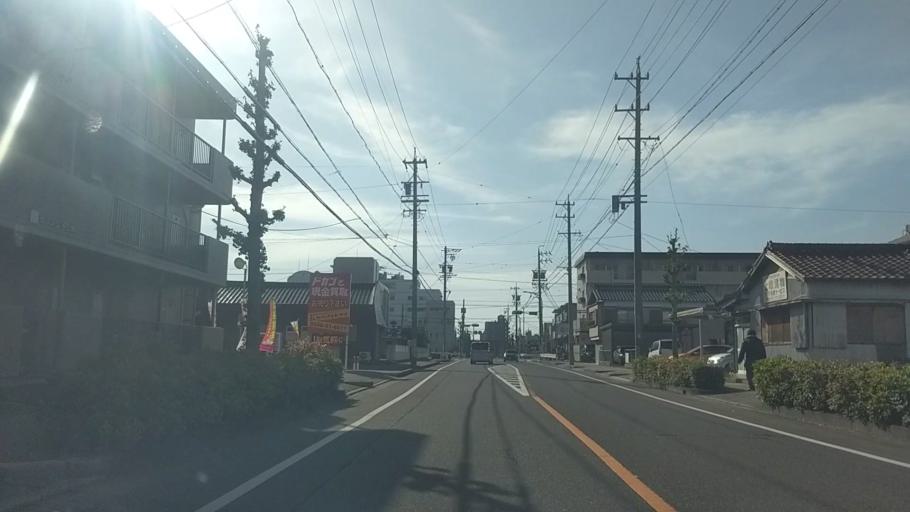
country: JP
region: Aichi
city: Anjo
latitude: 34.9547
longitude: 137.0960
